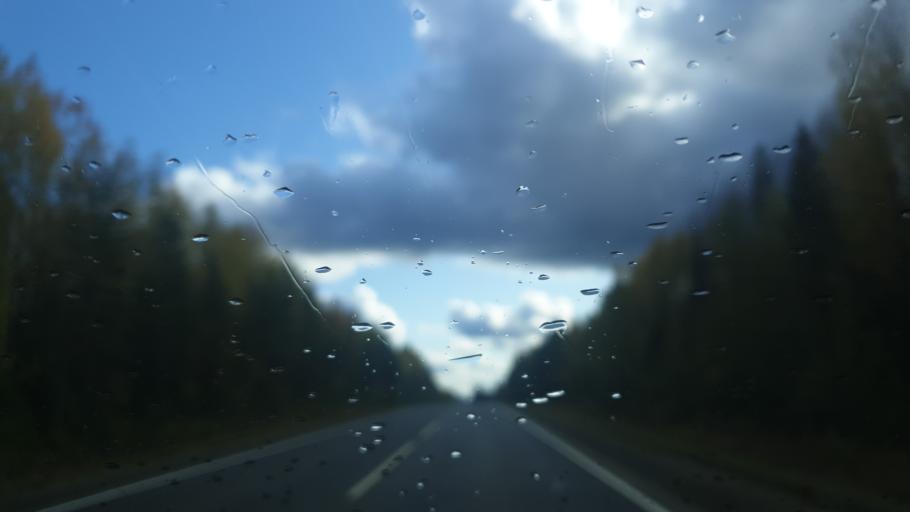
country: RU
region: Komi Republic
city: Vizinga
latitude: 60.4969
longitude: 49.6557
